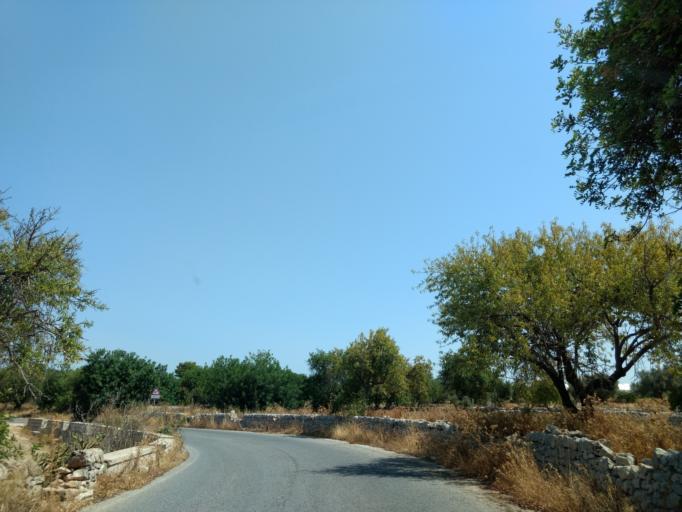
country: IT
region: Sicily
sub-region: Ragusa
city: Scicli
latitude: 36.7603
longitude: 14.7042
